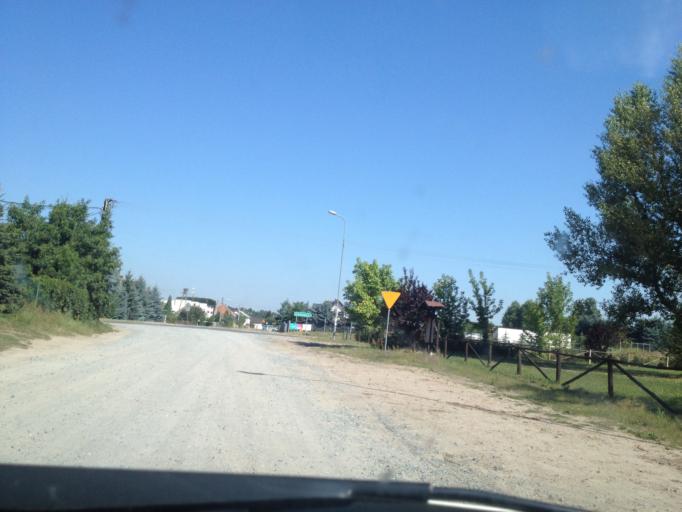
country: PL
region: Greater Poland Voivodeship
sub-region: Powiat sredzki
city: Zaniemysl
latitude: 52.1122
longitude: 17.1179
